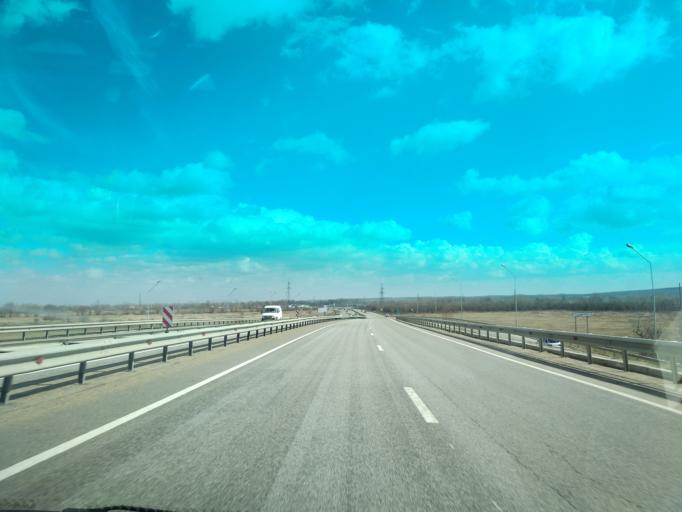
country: RU
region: Krasnodarskiy
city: Goryachiy Klyuch
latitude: 44.6454
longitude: 39.1325
